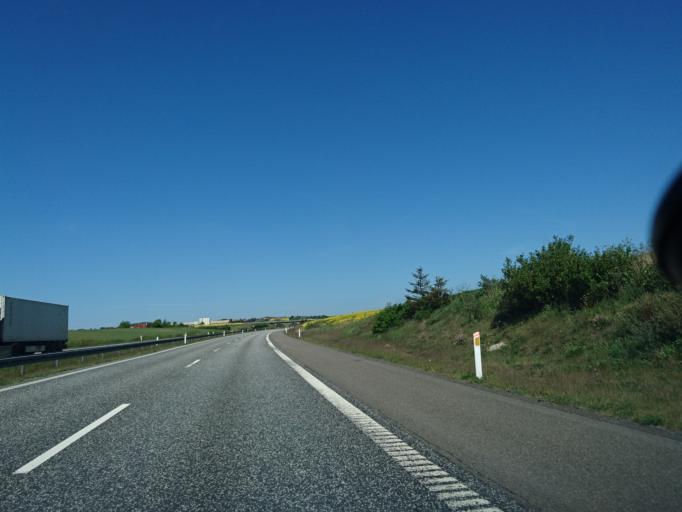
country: DK
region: North Denmark
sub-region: Hjorring Kommune
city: Hirtshals
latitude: 57.5378
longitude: 10.0080
